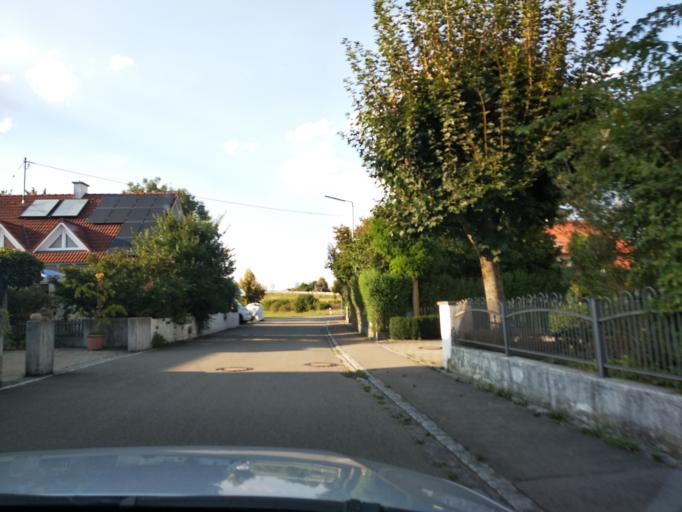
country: DE
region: Bavaria
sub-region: Swabia
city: Westerheim
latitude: 48.0224
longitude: 10.2958
